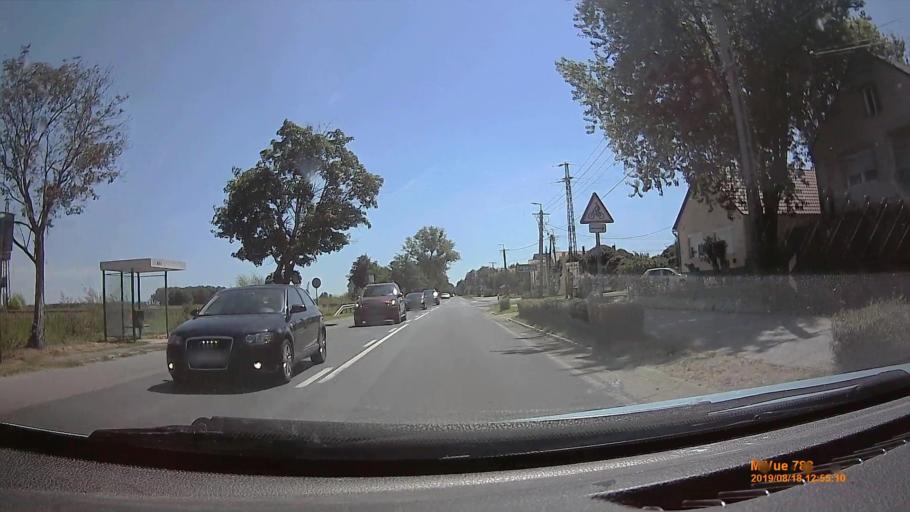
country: HU
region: Fejer
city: Aba
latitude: 47.0362
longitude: 18.5354
